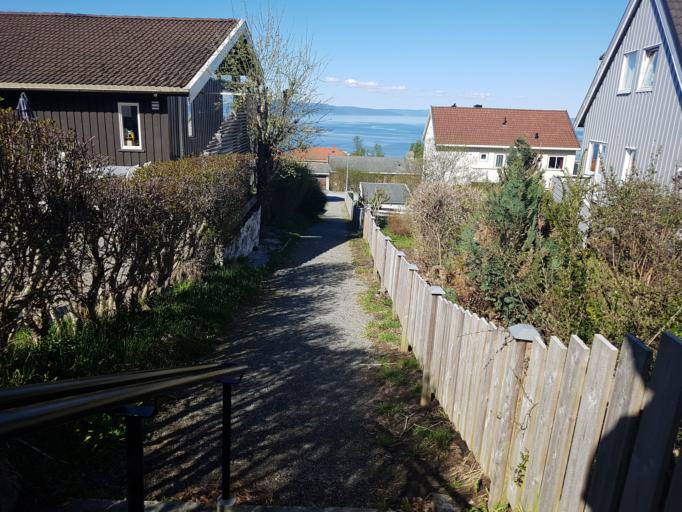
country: NO
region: Sor-Trondelag
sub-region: Trondheim
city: Trondheim
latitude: 63.4238
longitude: 10.3655
